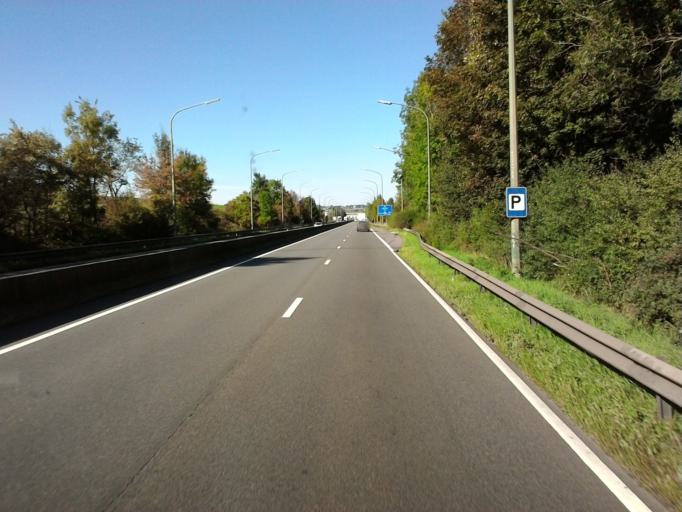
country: BE
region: Wallonia
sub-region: Province du Luxembourg
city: Messancy
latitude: 49.6003
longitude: 5.8086
